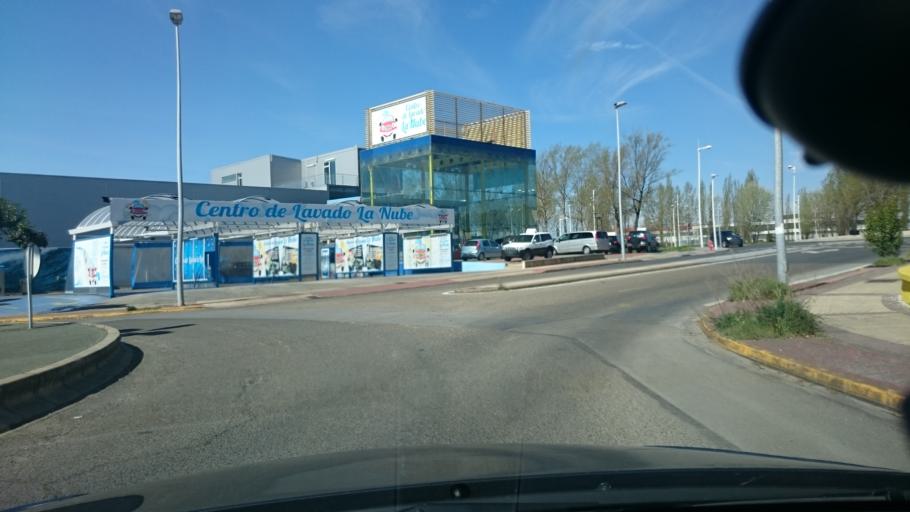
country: ES
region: Castille and Leon
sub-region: Provincia de Leon
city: Ponferrada
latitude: 42.5546
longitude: -6.6142
